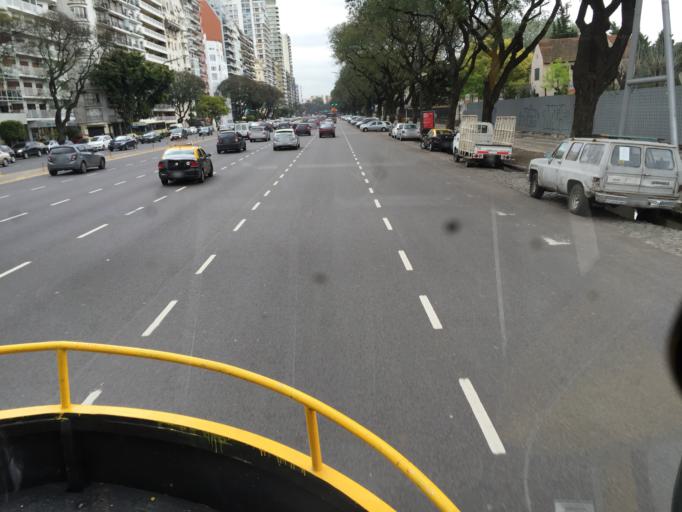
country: AR
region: Buenos Aires F.D.
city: Colegiales
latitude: -34.5672
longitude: -58.4302
